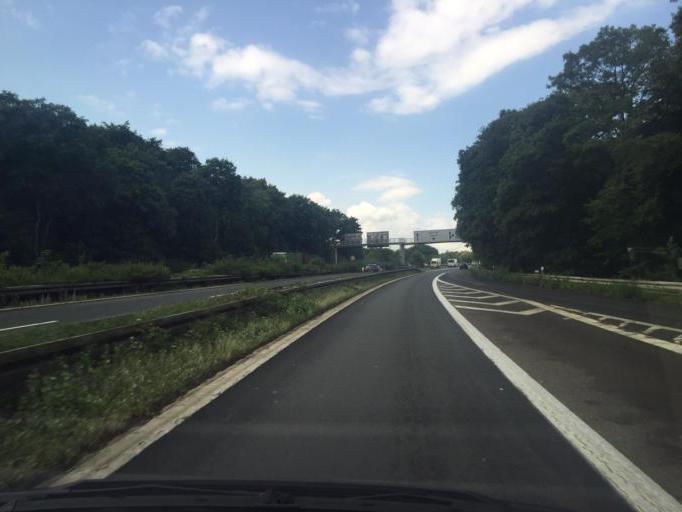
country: DE
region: North Rhine-Westphalia
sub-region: Regierungsbezirk Koln
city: Kalk
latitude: 50.9217
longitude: 7.0178
